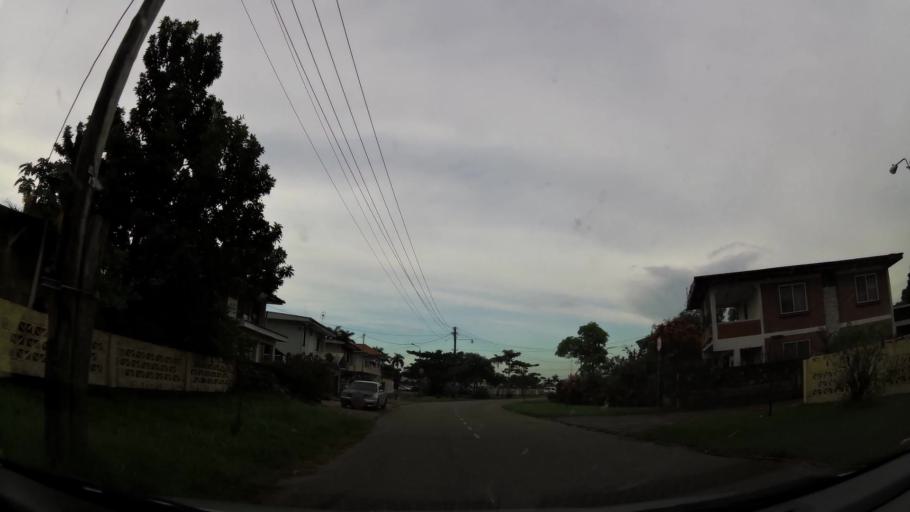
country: SR
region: Paramaribo
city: Paramaribo
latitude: 5.8149
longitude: -55.1993
